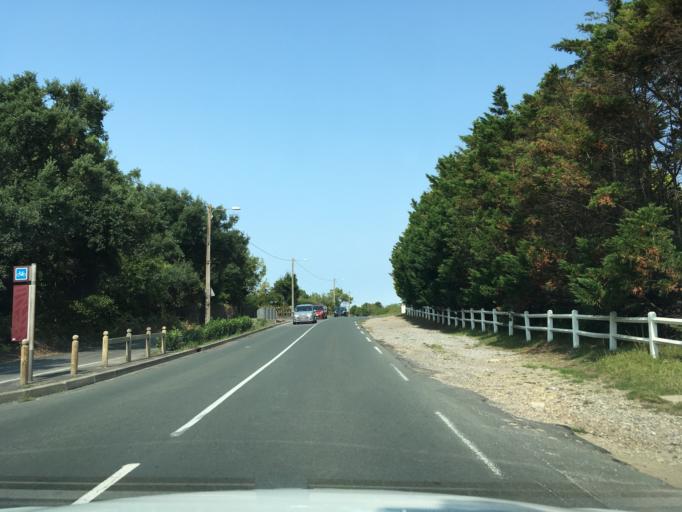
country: FR
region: Aquitaine
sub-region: Departement des Pyrenees-Atlantiques
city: Anglet
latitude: 43.5130
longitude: -1.5262
